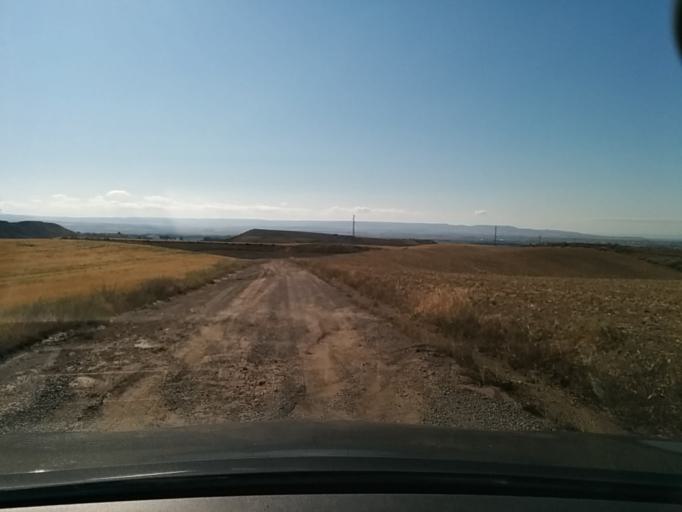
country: ES
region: Aragon
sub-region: Provincia de Zaragoza
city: Tauste
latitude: 42.0190
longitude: -1.3071
